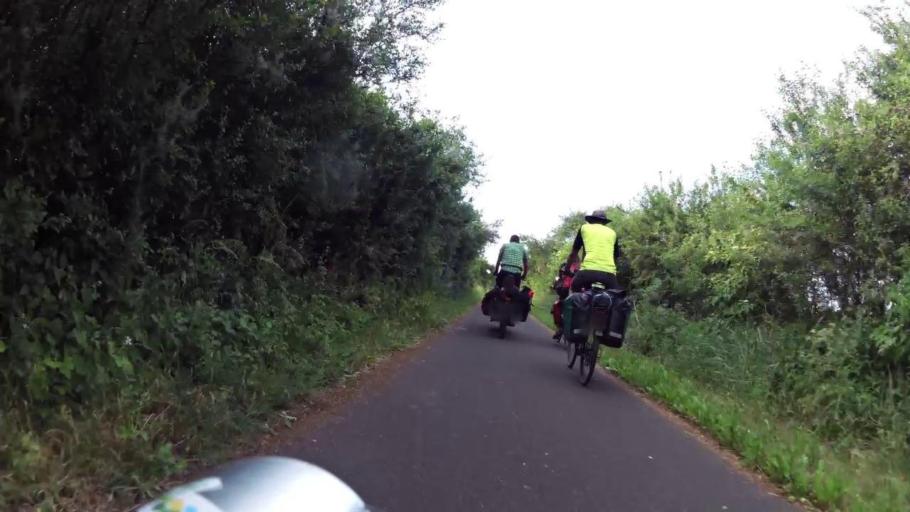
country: PL
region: Kujawsko-Pomorskie
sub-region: Powiat torunski
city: Lubianka
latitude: 53.1396
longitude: 18.4598
